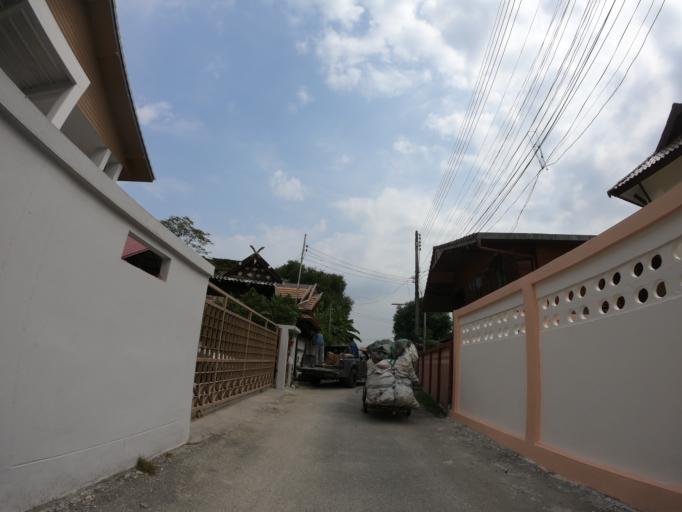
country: TH
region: Chiang Mai
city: Chiang Mai
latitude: 18.7759
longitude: 98.9845
